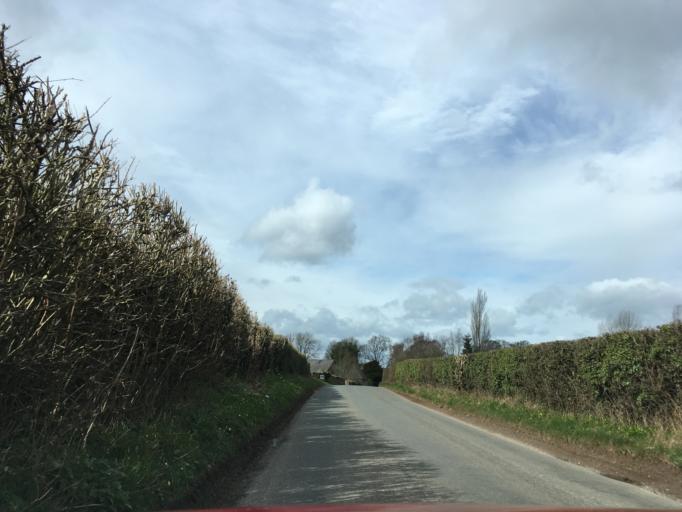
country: GB
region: England
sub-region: Gloucestershire
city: Coleford
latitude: 51.7645
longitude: -2.6191
